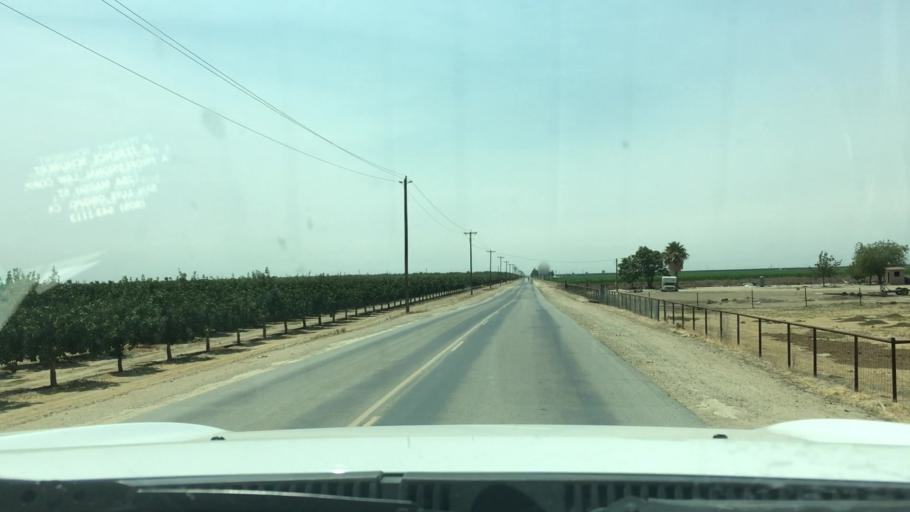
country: US
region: California
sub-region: Kern County
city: Wasco
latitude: 35.6802
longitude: -119.4374
